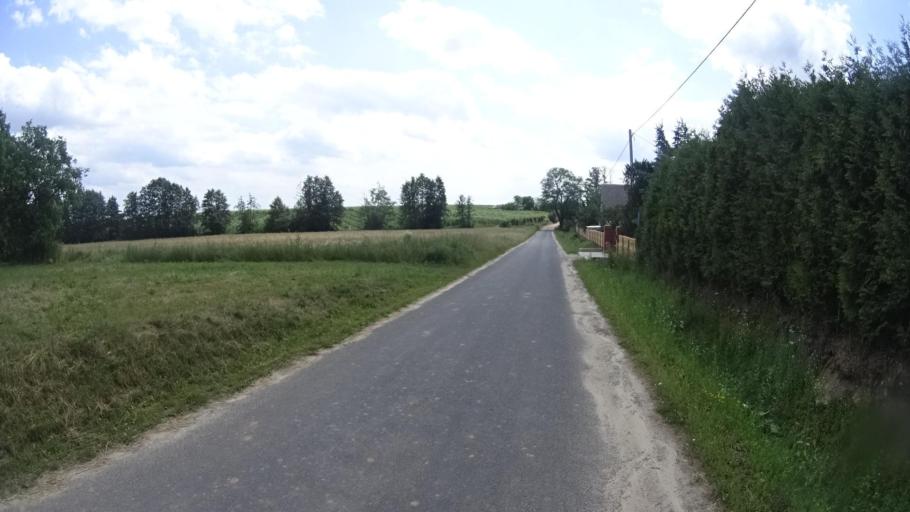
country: PL
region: Masovian Voivodeship
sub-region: Powiat grojecki
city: Goszczyn
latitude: 51.7132
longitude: 20.8321
